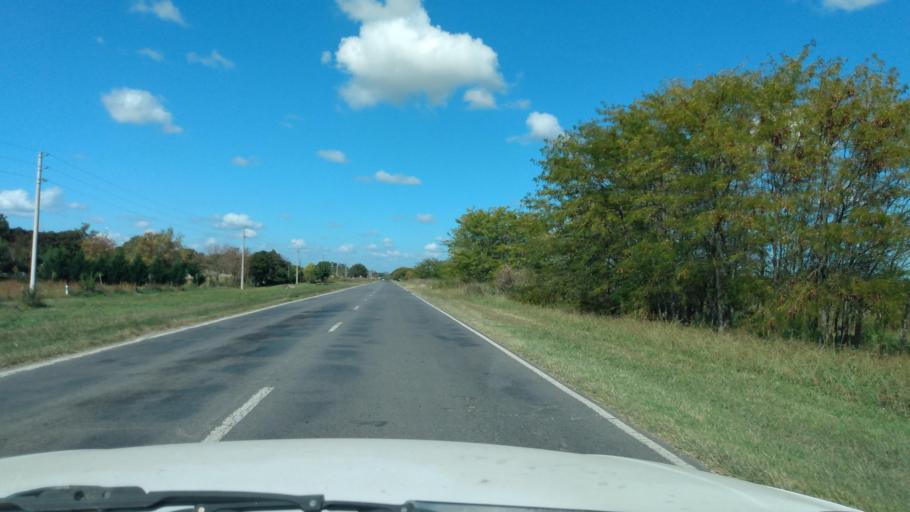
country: AR
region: Buenos Aires
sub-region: Partido de Mercedes
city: Mercedes
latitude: -34.6928
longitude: -59.4043
